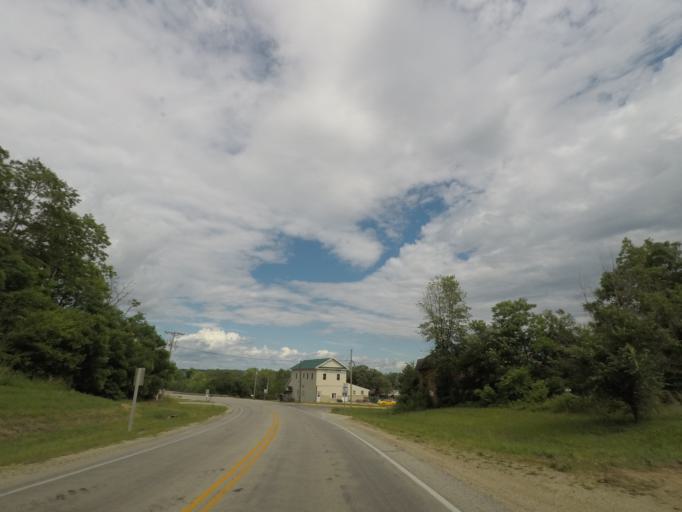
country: US
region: Wisconsin
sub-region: Dane County
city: Belleville
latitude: 42.8273
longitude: -89.5122
